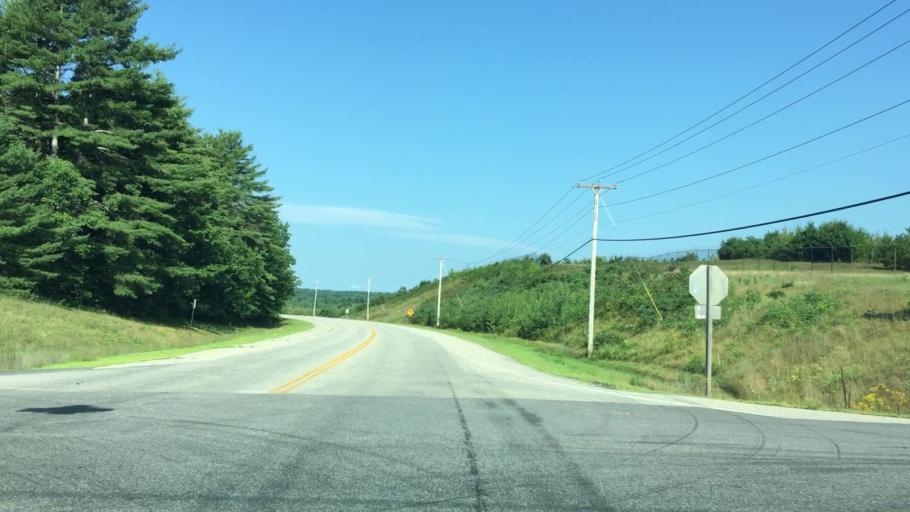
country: US
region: Maine
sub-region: Androscoggin County
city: Minot
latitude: 44.0402
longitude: -70.2796
